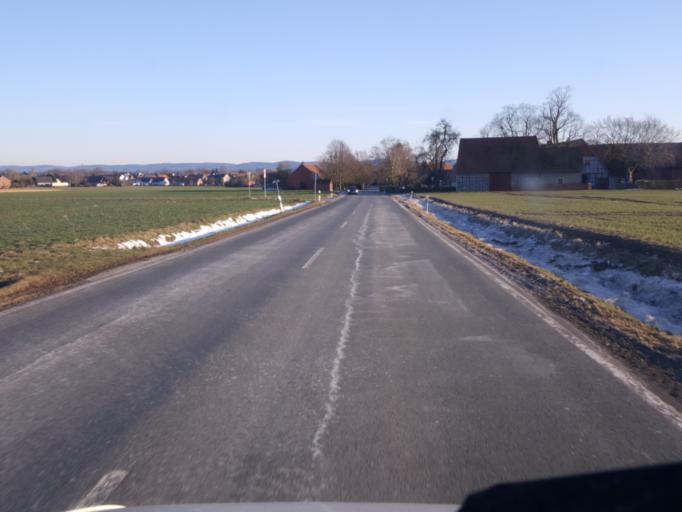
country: DE
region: North Rhine-Westphalia
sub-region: Regierungsbezirk Detmold
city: Hille
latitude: 52.3480
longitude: 8.7327
